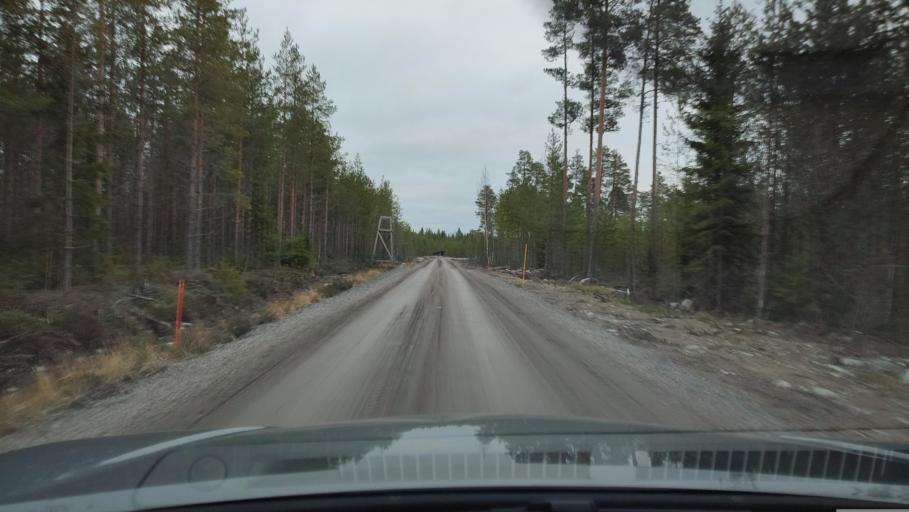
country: FI
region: Southern Ostrobothnia
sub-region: Suupohja
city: Karijoki
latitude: 62.1892
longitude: 21.5658
